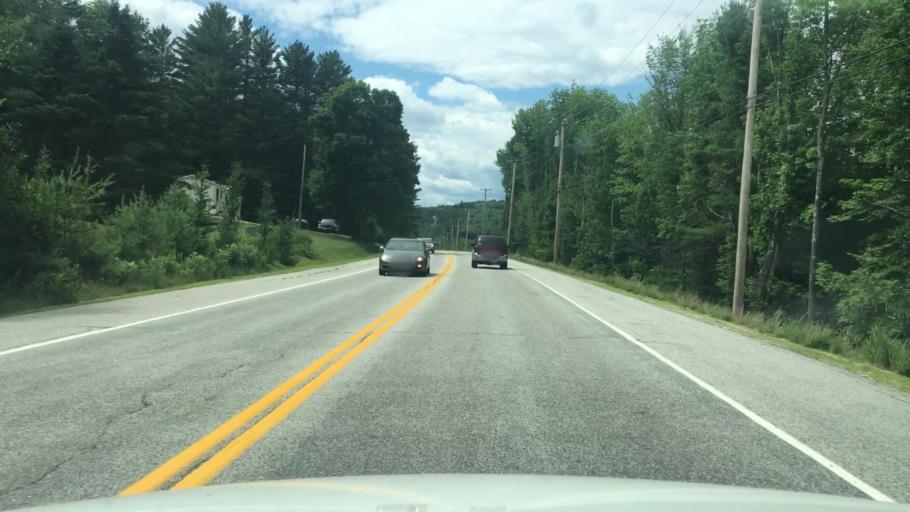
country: US
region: Maine
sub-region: Oxford County
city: West Paris
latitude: 44.3826
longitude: -70.6212
